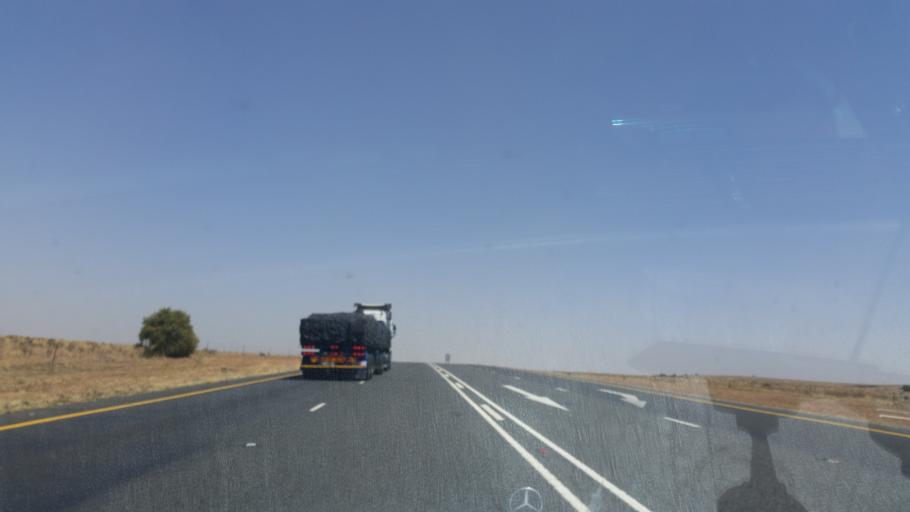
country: ZA
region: Orange Free State
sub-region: Lejweleputswa District Municipality
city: Winburg
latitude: -28.7056
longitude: 26.7914
